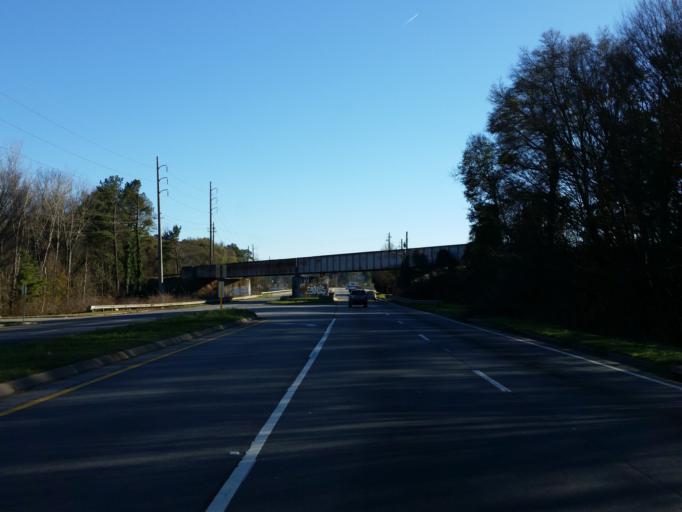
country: US
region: Georgia
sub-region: Cobb County
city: Vinings
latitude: 33.8288
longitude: -84.4599
